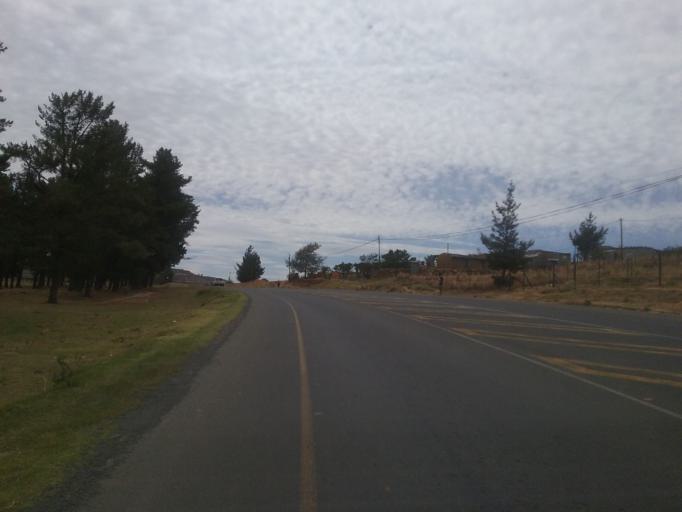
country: LS
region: Maseru
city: Nako
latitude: -29.6293
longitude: 27.4853
